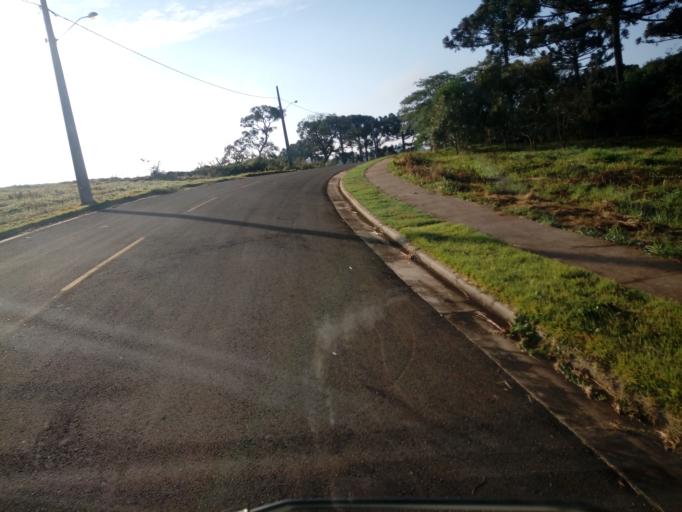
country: BR
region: Santa Catarina
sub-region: Chapeco
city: Chapeco
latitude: -27.0908
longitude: -52.7092
